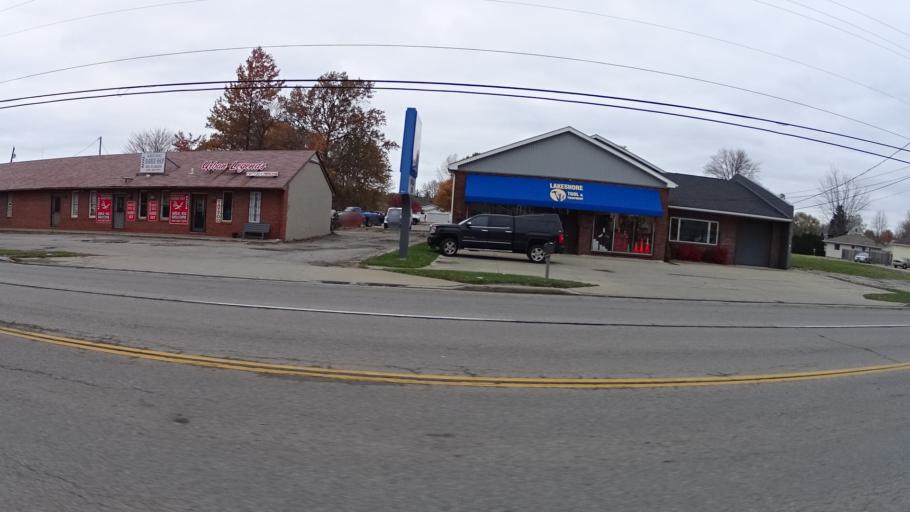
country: US
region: Ohio
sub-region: Lorain County
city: Sheffield
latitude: 41.4183
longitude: -82.1259
